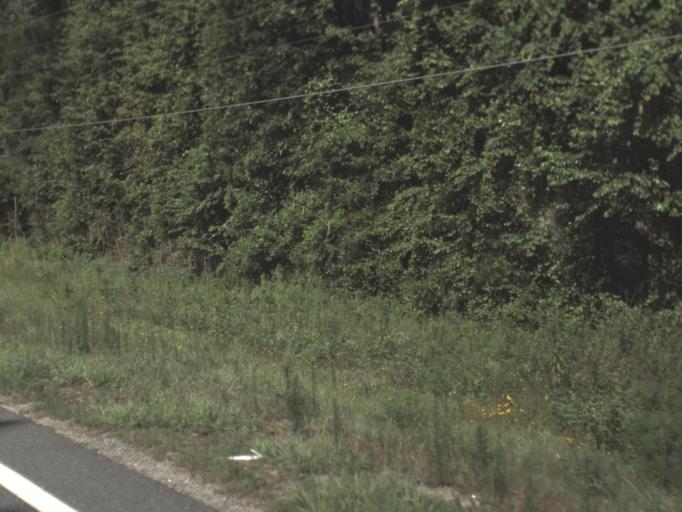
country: US
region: Florida
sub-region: Madison County
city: Madison
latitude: 30.5151
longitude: -83.3711
